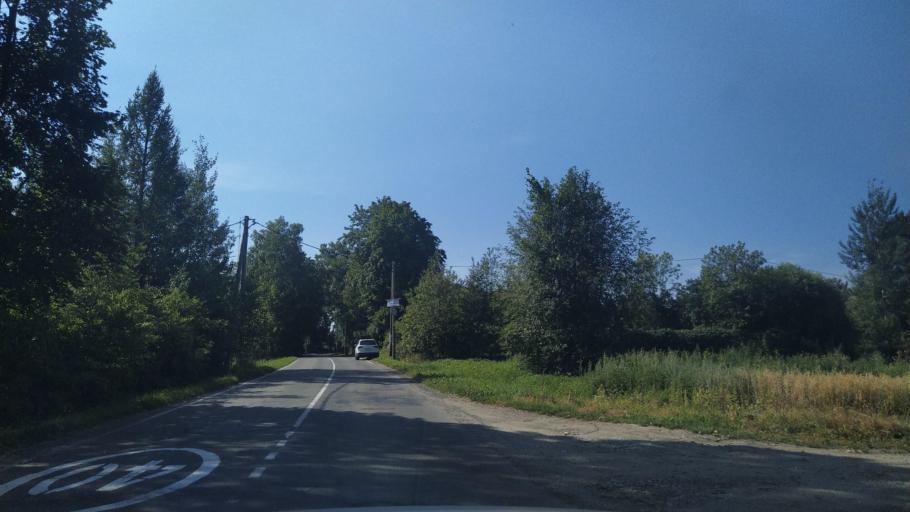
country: RU
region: Leningrad
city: Siverskiy
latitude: 59.2977
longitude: 30.0745
